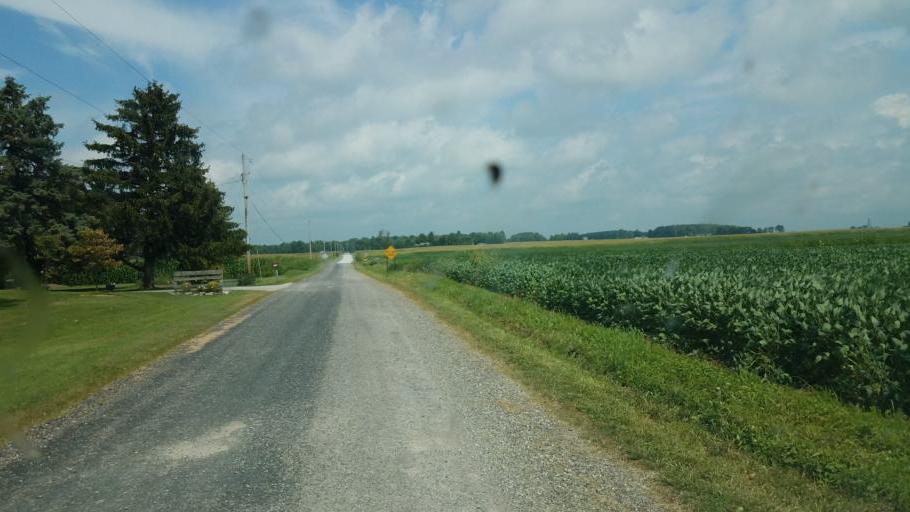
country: US
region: Ohio
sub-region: Morrow County
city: Mount Gilead
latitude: 40.6061
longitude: -82.7095
